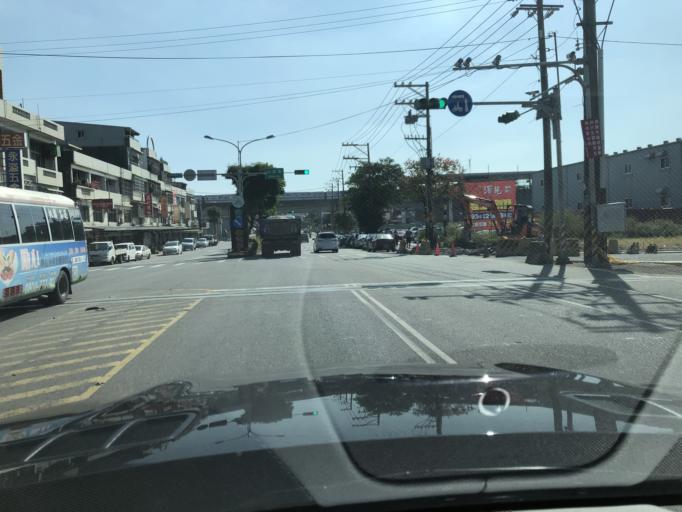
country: TW
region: Taiwan
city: Taoyuan City
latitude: 25.0825
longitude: 121.2859
